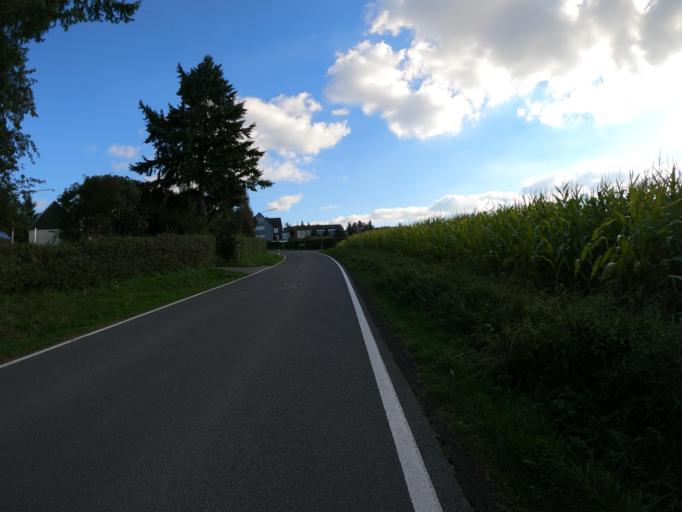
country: DE
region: North Rhine-Westphalia
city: Radevormwald
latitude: 51.2312
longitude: 7.3373
